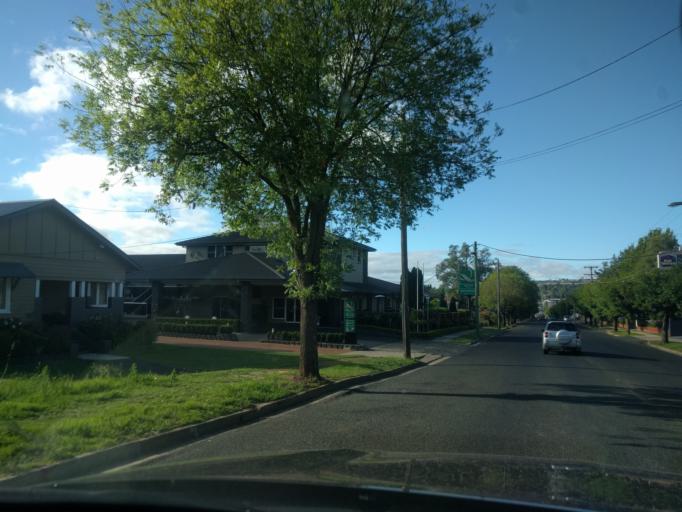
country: AU
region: New South Wales
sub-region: Armidale Dumaresq
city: Armidale
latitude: -30.5056
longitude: 151.6722
